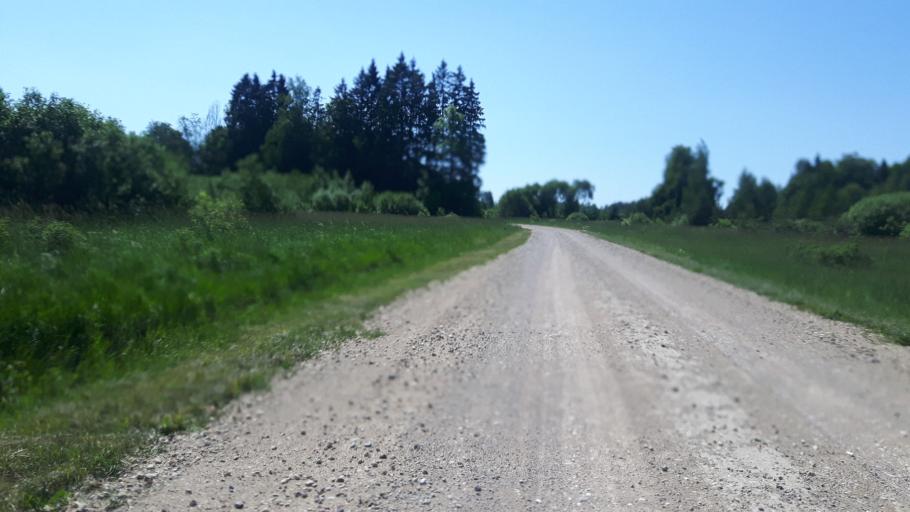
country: EE
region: Paernumaa
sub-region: Vaendra vald (alev)
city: Vandra
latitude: 58.5581
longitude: 24.9510
